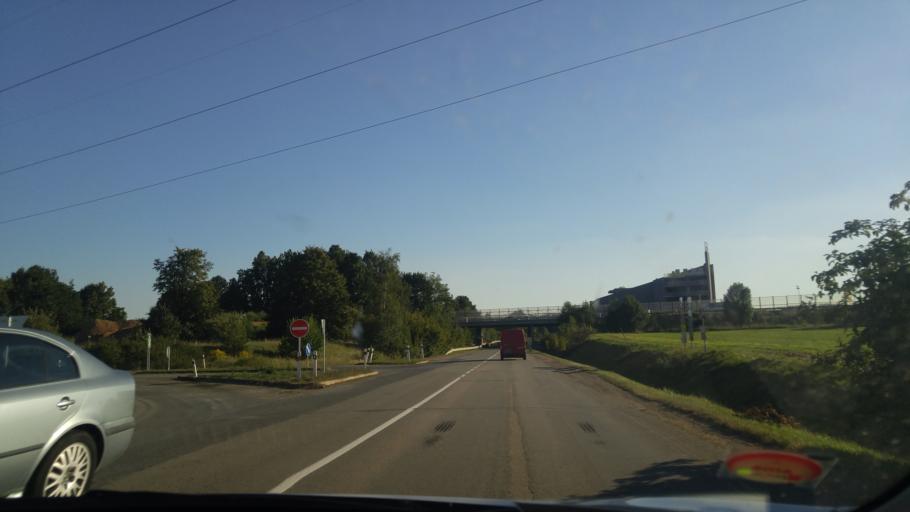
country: CZ
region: South Moravian
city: Ricany
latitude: 49.2176
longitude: 16.4117
